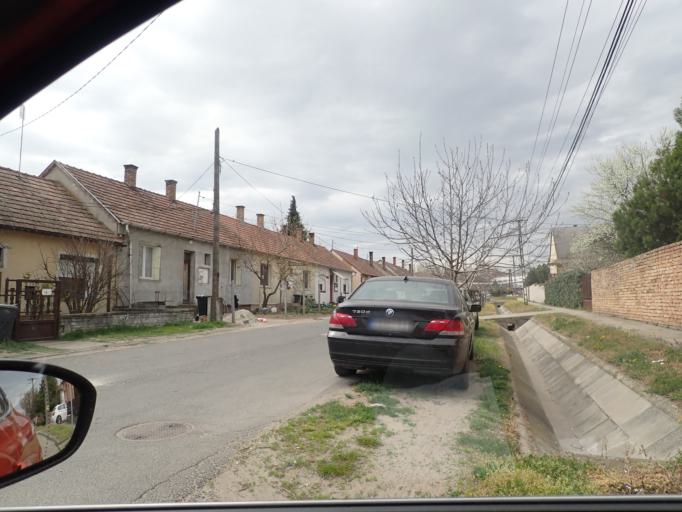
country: HU
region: Tolna
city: Paks
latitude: 46.6064
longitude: 18.8457
